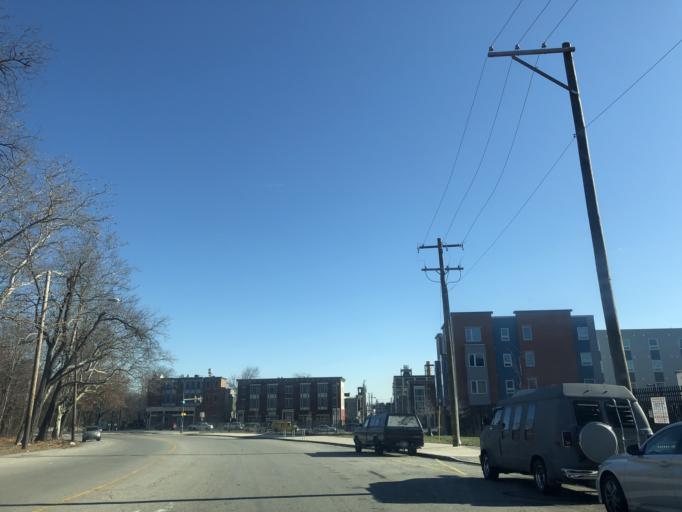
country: US
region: Pennsylvania
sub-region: Montgomery County
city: Bala-Cynwyd
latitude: 39.9815
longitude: -75.2257
